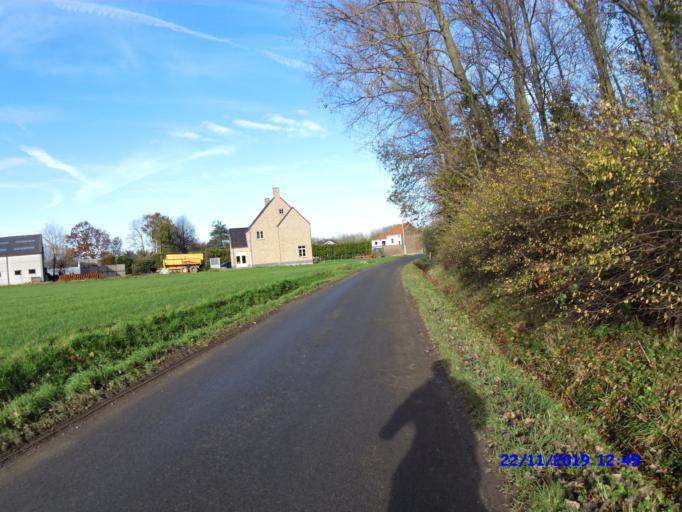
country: BE
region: Flanders
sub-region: Provincie Vlaams-Brabant
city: Merchtem
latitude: 50.9723
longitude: 4.2714
